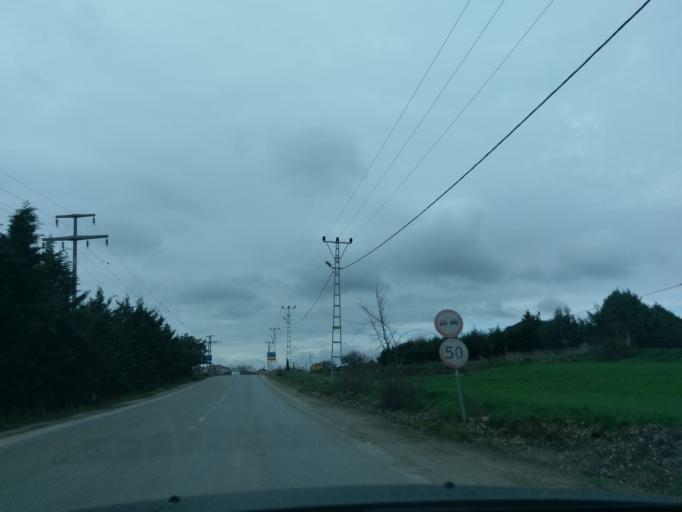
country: TR
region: Istanbul
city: Catalca
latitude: 41.1875
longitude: 28.4085
